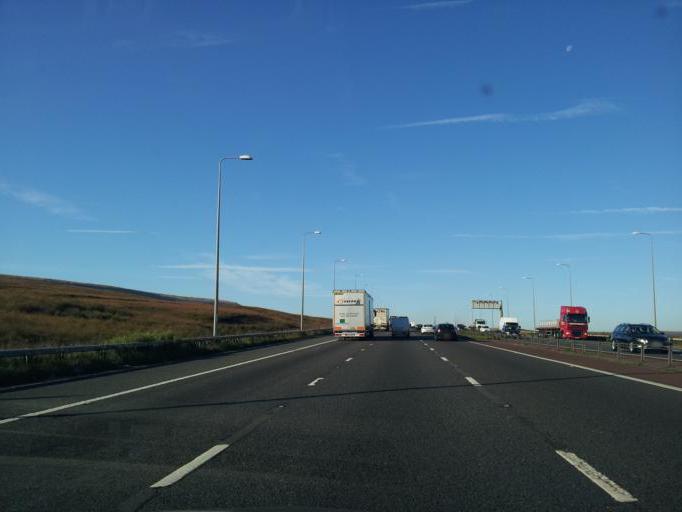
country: GB
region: England
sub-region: Calderdale
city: Ripponden
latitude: 53.6372
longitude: -1.9775
